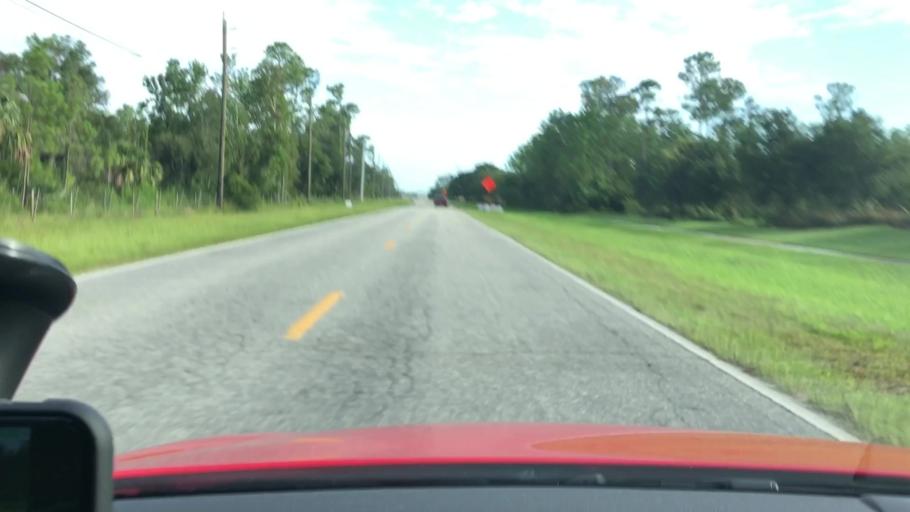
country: US
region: Florida
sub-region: Volusia County
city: Daytona Beach
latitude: 29.1769
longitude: -81.0906
